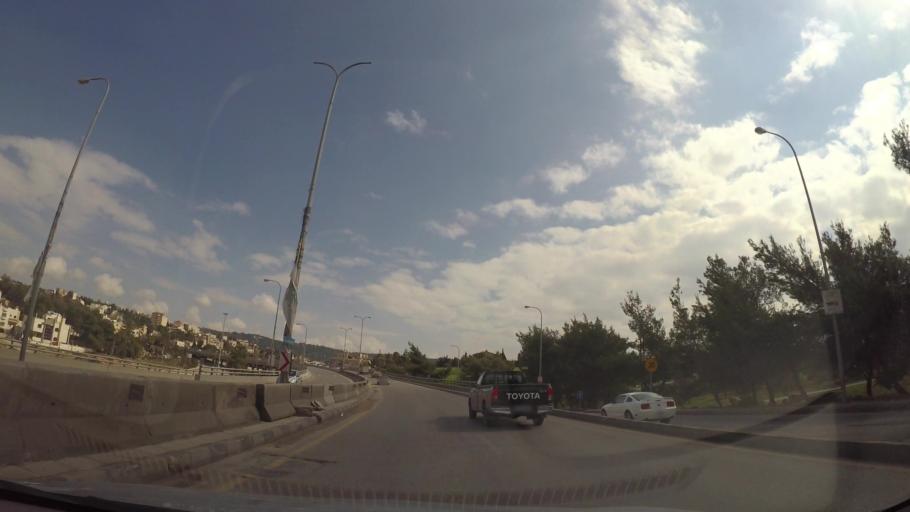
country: JO
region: Amman
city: Al Jubayhah
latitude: 32.0287
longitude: 35.7970
